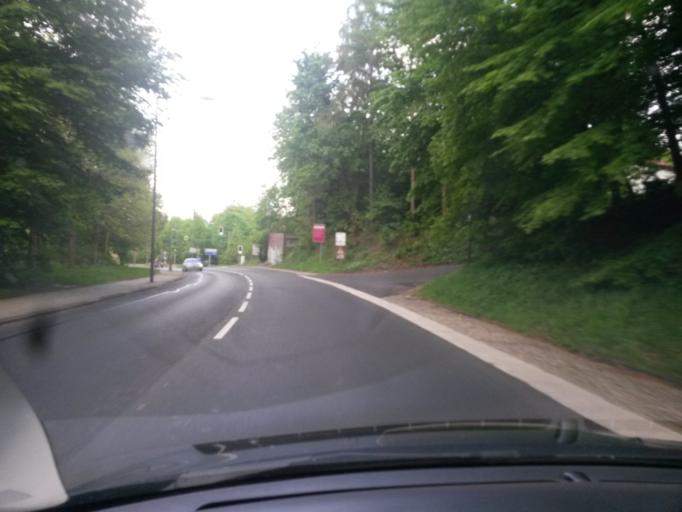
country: DE
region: Hesse
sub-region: Regierungsbezirk Kassel
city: Baunatal
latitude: 51.3017
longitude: 9.4116
